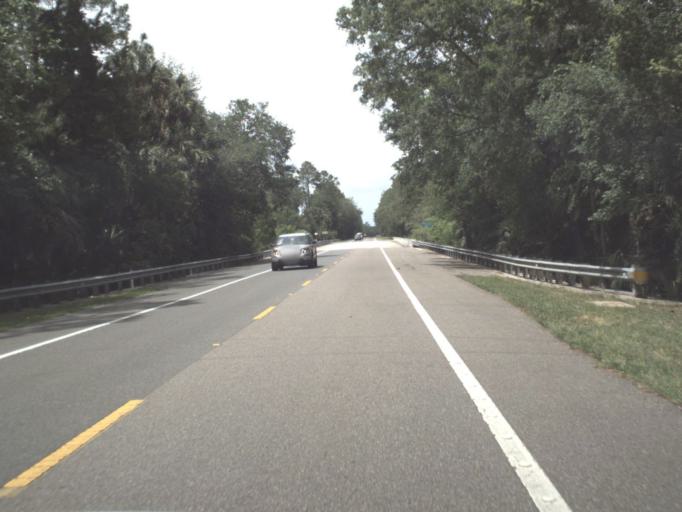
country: US
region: Florida
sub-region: Flagler County
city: Bunnell
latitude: 29.3586
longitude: -81.3114
